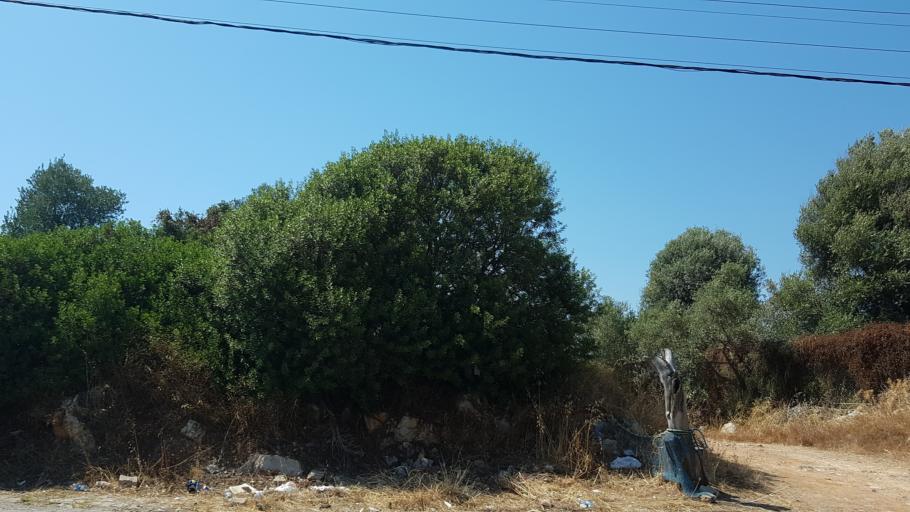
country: TR
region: Mugla
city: Karaova
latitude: 37.1345
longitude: 27.5811
